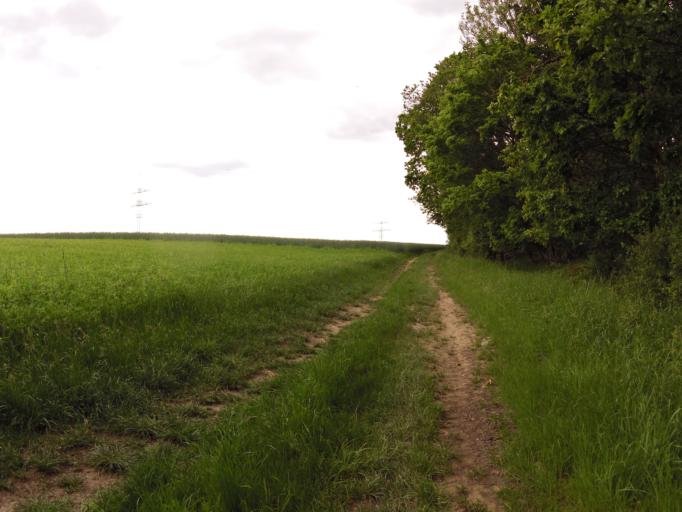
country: DE
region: Bavaria
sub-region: Regierungsbezirk Unterfranken
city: Theilheim
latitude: 49.7257
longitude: 10.0556
